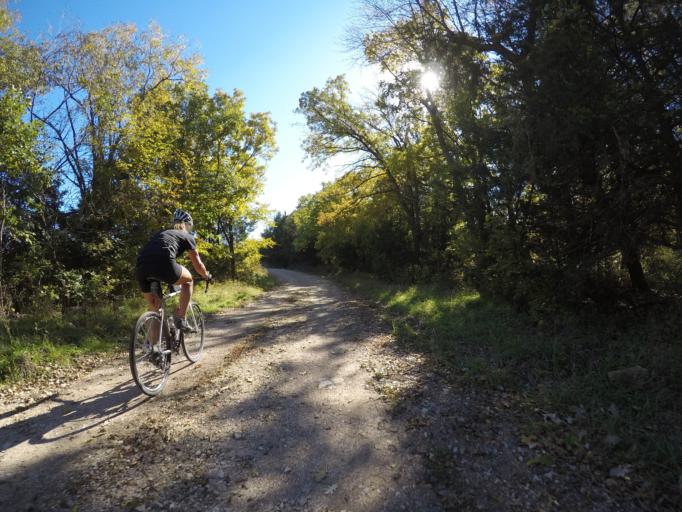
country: US
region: Kansas
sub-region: Wabaunsee County
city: Alma
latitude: 38.9787
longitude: -96.4555
